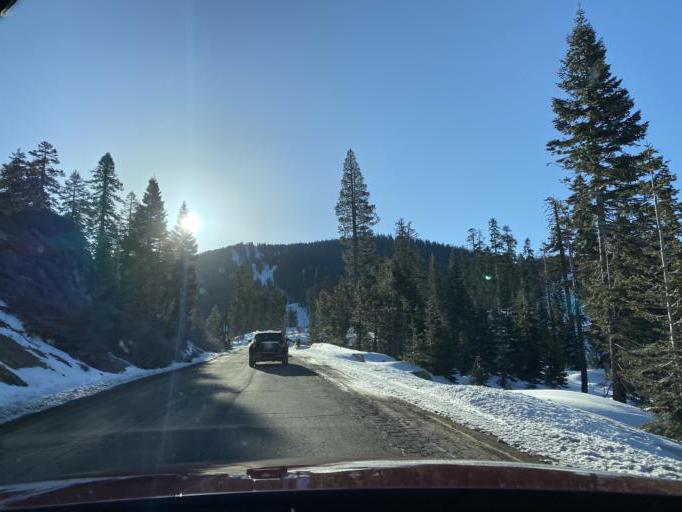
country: US
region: California
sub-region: El Dorado County
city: South Lake Tahoe
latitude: 38.8042
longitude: -120.0855
